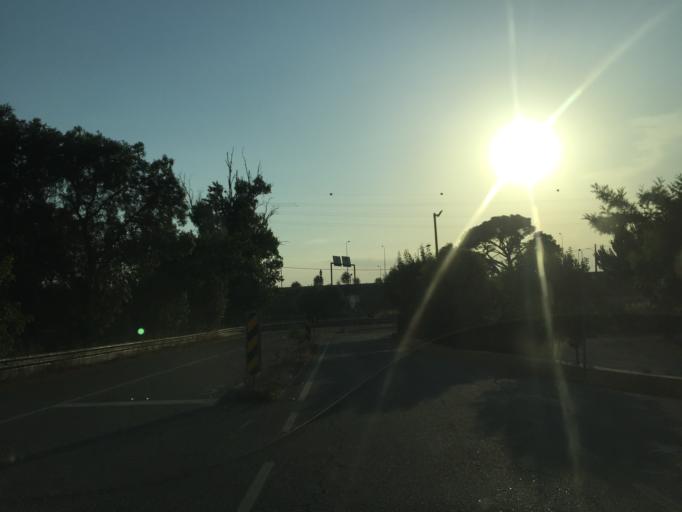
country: PT
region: Santarem
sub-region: Tomar
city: Tomar
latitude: 39.5509
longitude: -8.3884
